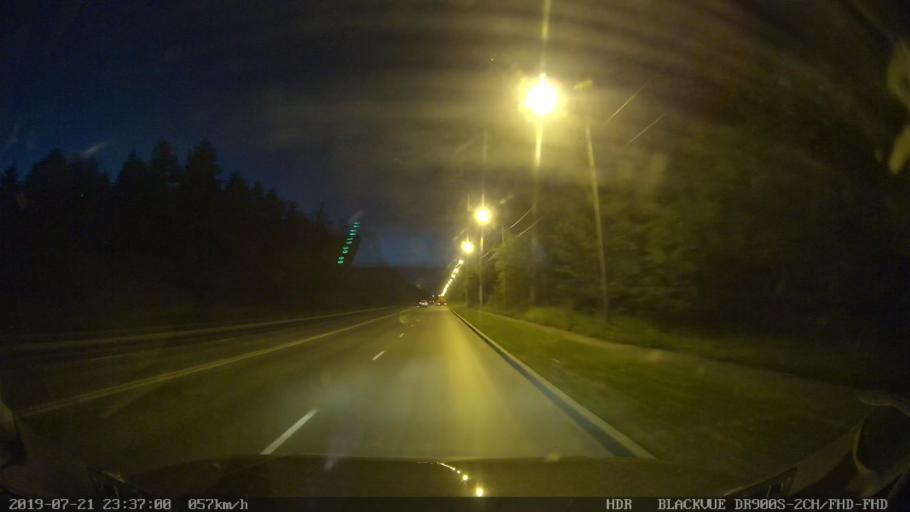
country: RU
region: Perm
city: Kondratovo
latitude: 57.9440
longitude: 56.1716
